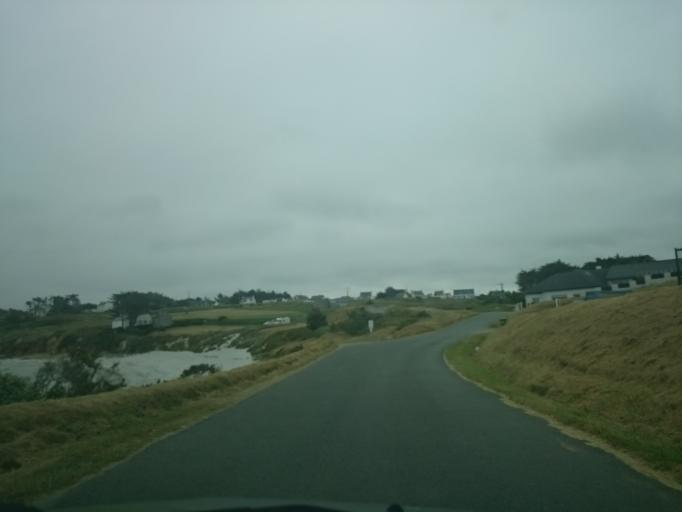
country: FR
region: Brittany
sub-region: Departement du Finistere
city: Saint-Pabu
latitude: 48.5757
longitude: -4.6265
